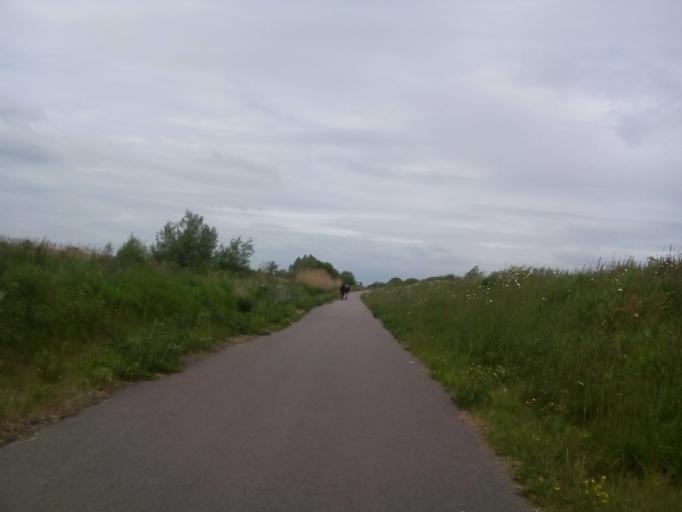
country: GB
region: England
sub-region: Cambridgeshire
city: Swavesey
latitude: 52.3074
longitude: -0.0229
